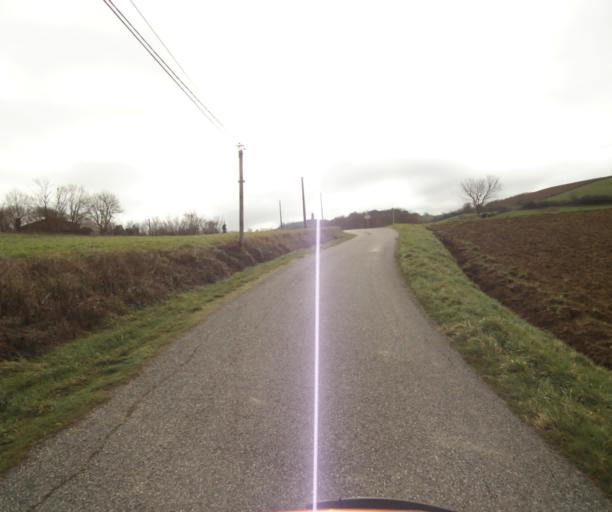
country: FR
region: Midi-Pyrenees
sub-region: Departement de l'Ariege
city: Saverdun
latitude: 43.1685
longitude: 1.5084
